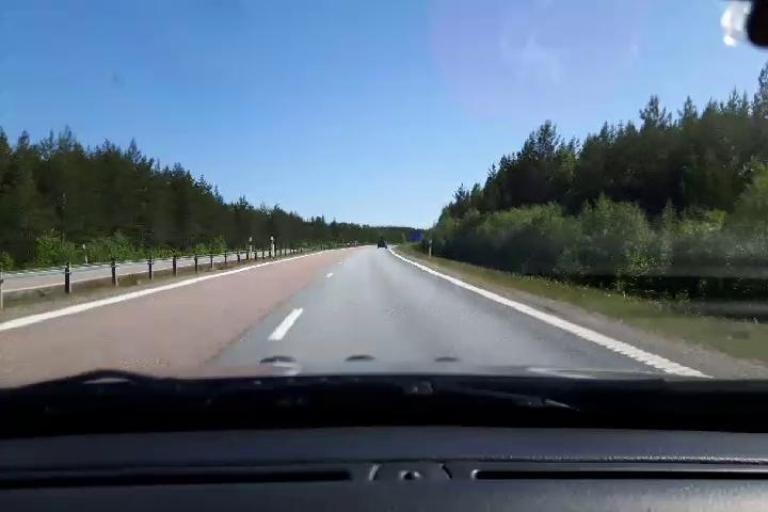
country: SE
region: Gaevleborg
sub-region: Soderhamns Kommun
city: Soderhamn
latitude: 61.4121
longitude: 16.9916
